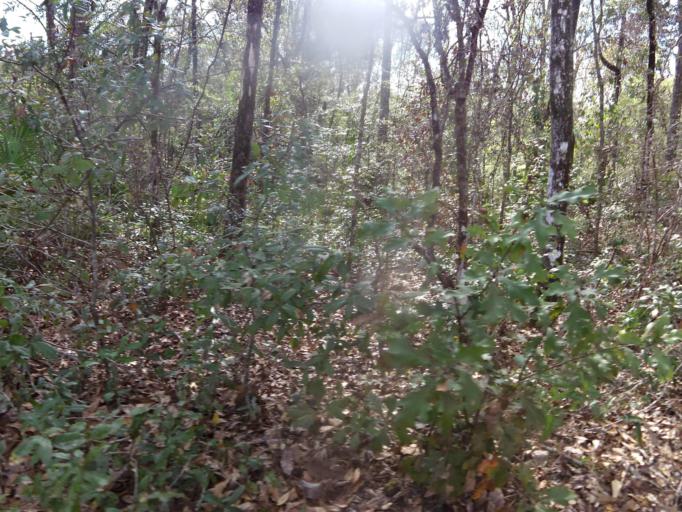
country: US
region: Florida
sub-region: Putnam County
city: Interlachen
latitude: 29.7610
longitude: -81.8220
